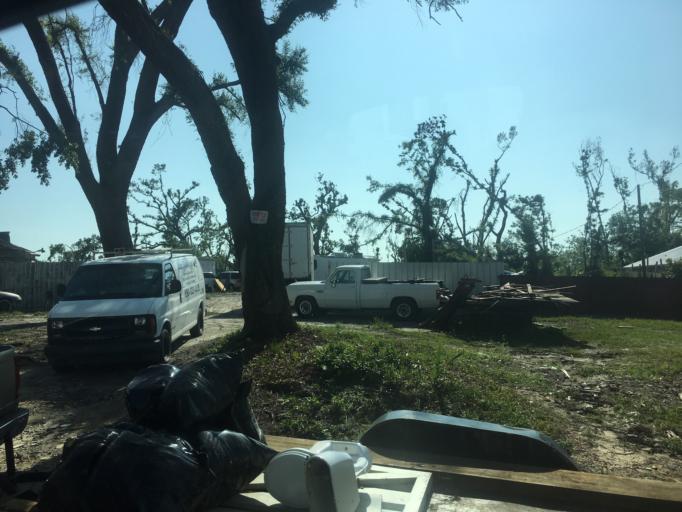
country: US
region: Florida
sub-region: Bay County
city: Springfield
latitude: 30.1483
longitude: -85.6191
